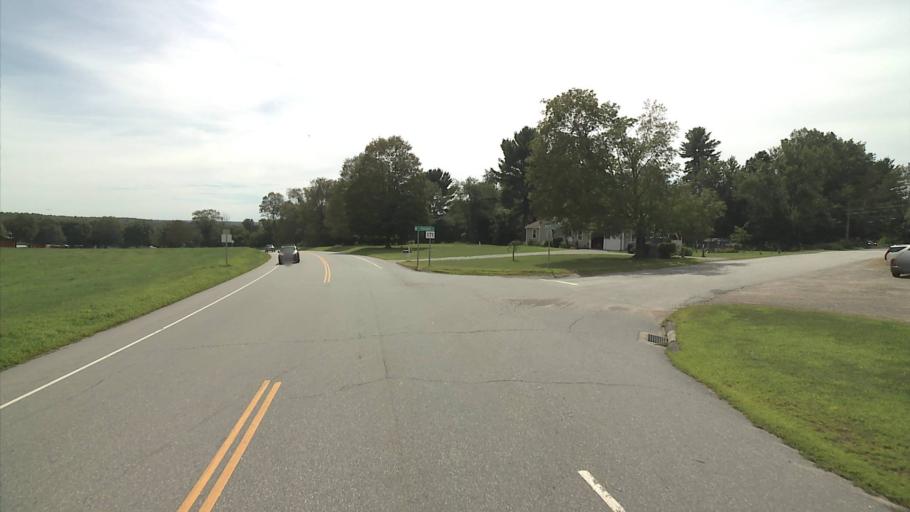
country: US
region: Connecticut
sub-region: Windham County
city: South Woodstock
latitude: 41.9331
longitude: -71.9553
